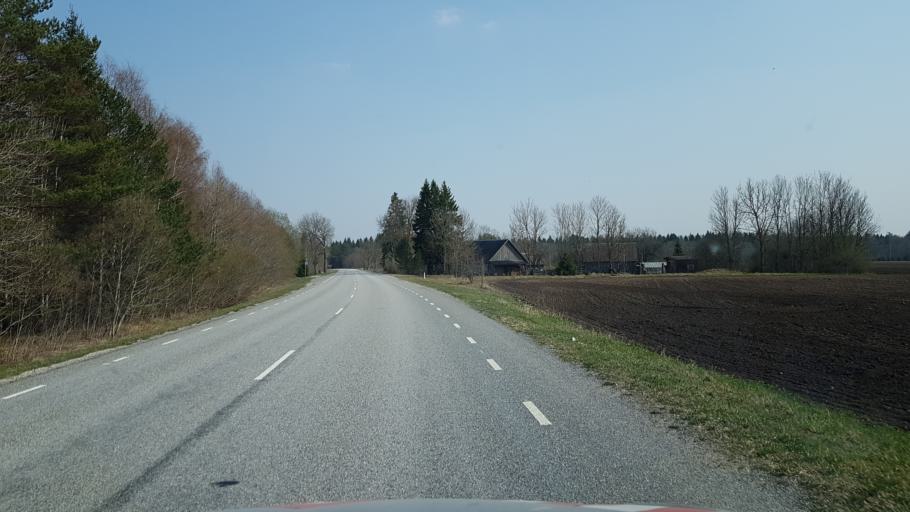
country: EE
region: Harju
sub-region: Paldiski linn
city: Paldiski
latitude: 59.2362
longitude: 23.9476
